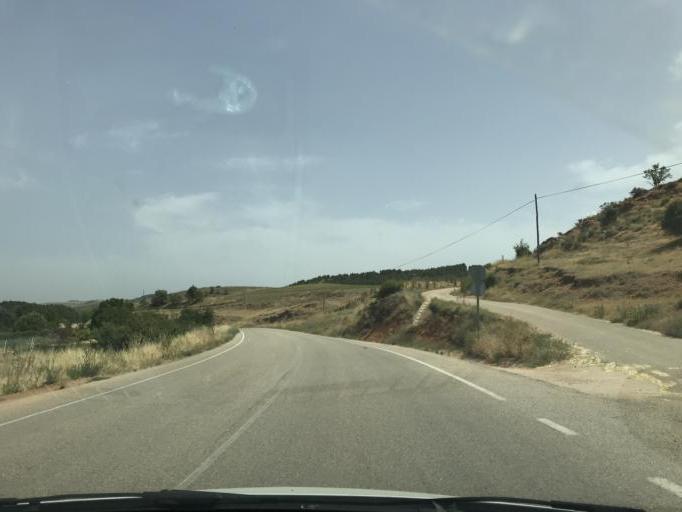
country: ES
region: Castille-La Mancha
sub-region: Provincia de Cuenca
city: Torralba
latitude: 40.3072
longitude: -2.2791
